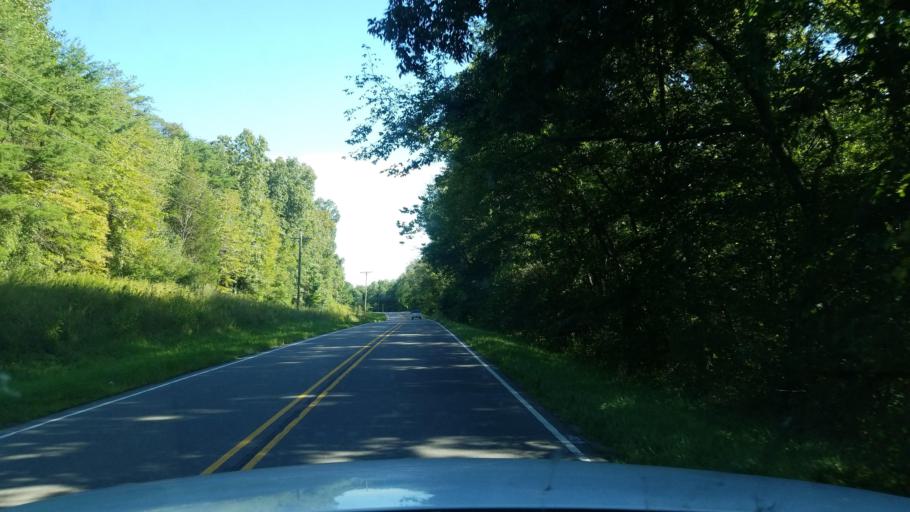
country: US
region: Illinois
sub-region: Saline County
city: Harrisburg
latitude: 37.6087
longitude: -88.4632
